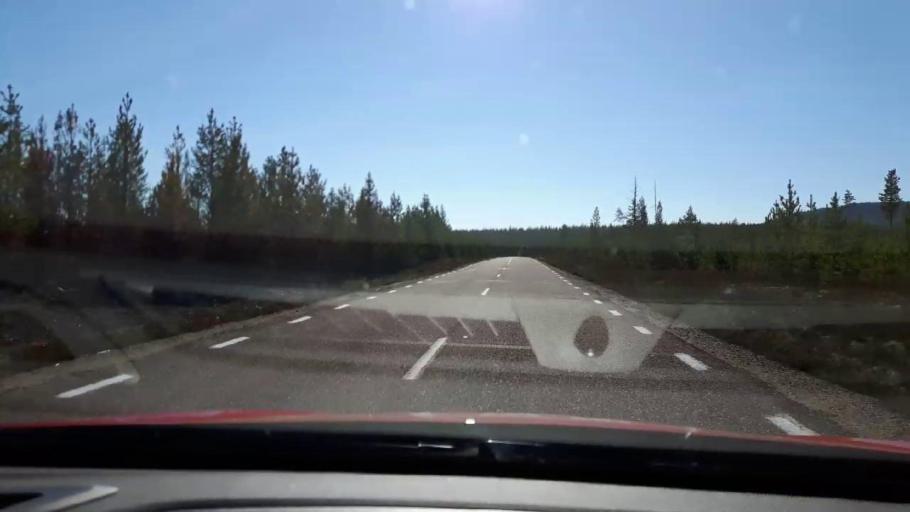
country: SE
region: Jaemtland
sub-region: Harjedalens Kommun
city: Sveg
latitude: 61.7151
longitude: 14.1686
